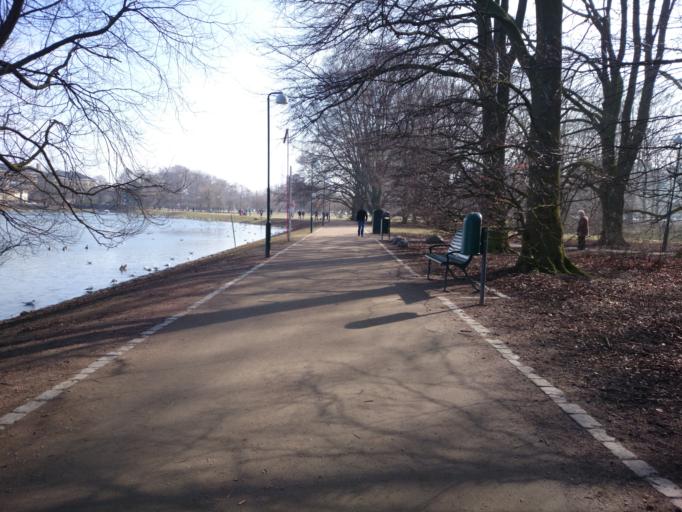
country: SE
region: Skane
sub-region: Malmo
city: Malmoe
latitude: 55.5883
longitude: 12.9950
